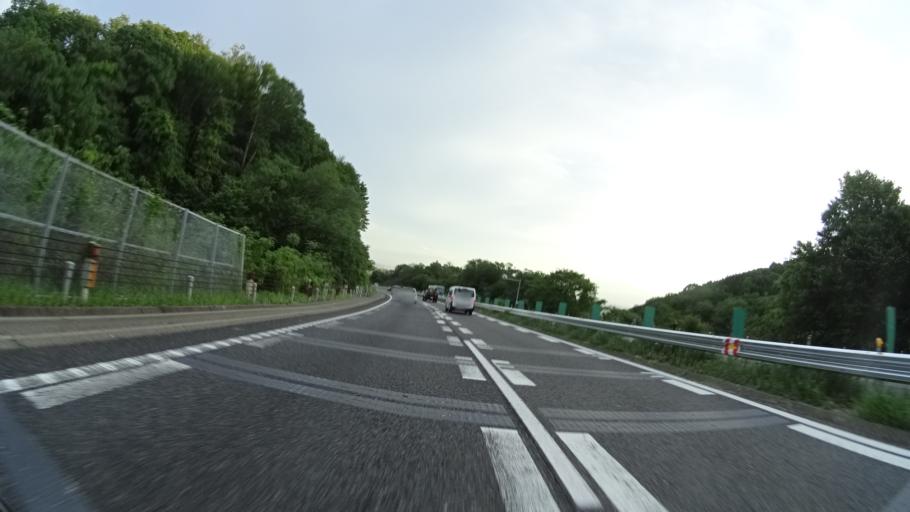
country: JP
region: Aichi
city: Kasugai
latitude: 35.3216
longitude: 137.0202
